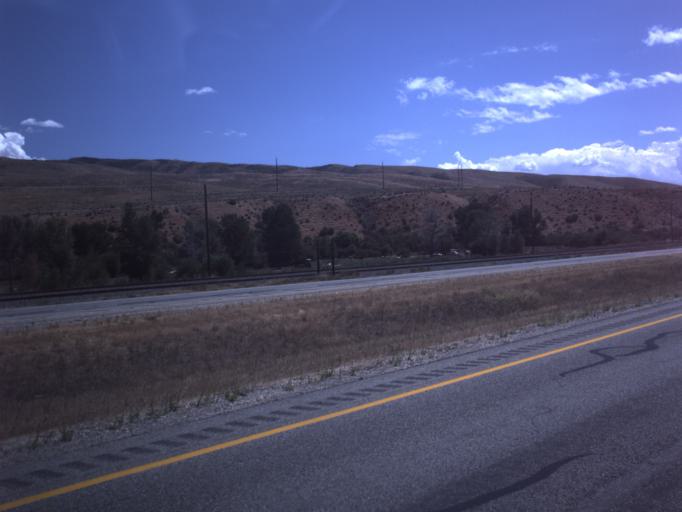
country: US
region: Utah
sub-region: Summit County
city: Coalville
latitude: 41.0238
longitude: -111.4963
